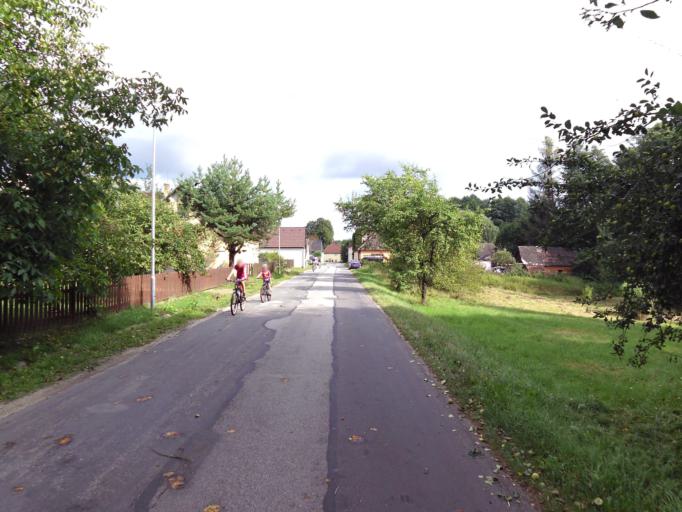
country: CZ
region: Jihocesky
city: Suchdol nad Luznici
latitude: 48.9063
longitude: 14.9097
